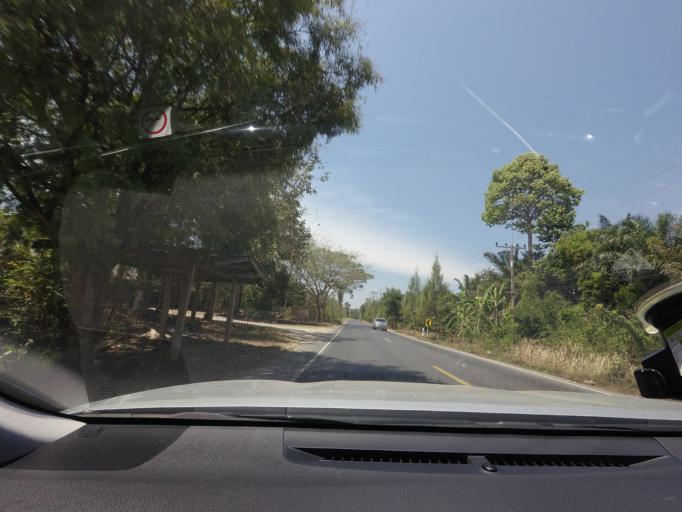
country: TH
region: Surat Thani
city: Tha Chang
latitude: 9.2621
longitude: 99.1772
